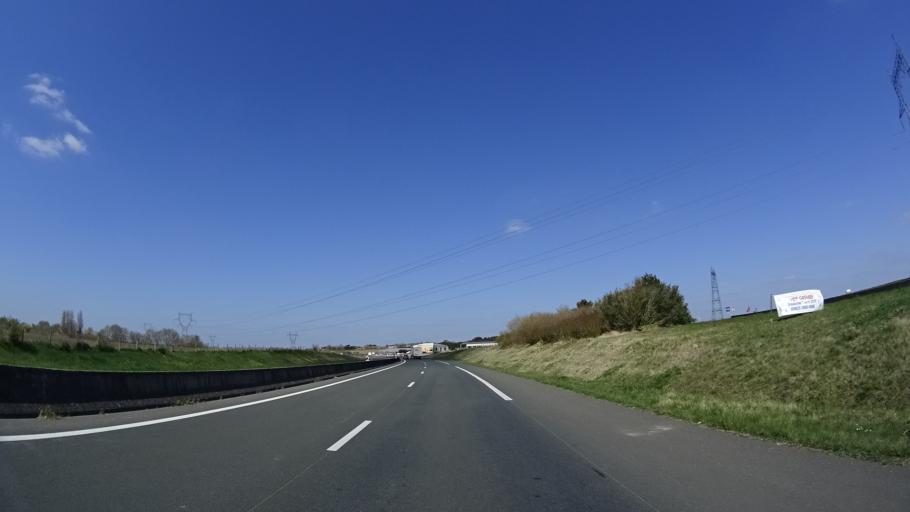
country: FR
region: Pays de la Loire
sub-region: Departement de Maine-et-Loire
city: Doue-la-Fontaine
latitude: 47.2295
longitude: -0.3094
